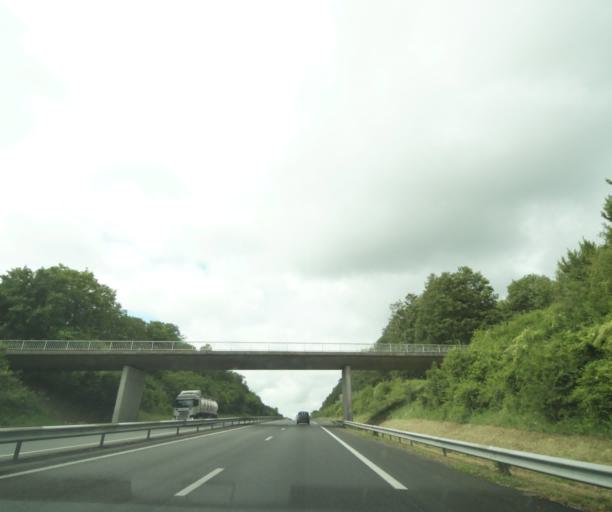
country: FR
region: Pays de la Loire
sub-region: Departement de Maine-et-Loire
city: Seiches-sur-le-Loir
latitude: 47.6082
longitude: -0.3010
